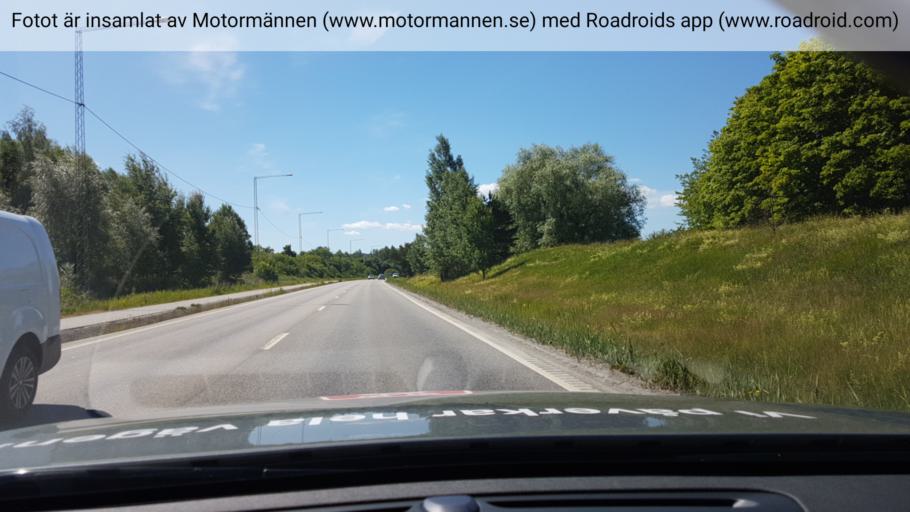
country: SE
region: Stockholm
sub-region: Haninge Kommun
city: Haninge
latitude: 59.1858
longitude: 18.1721
